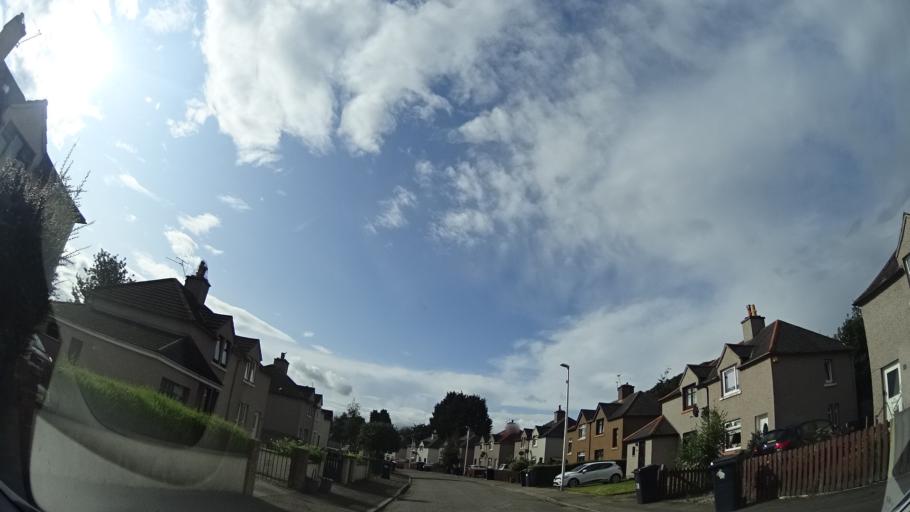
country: GB
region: Scotland
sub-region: Highland
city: Inverness
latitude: 57.4709
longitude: -4.2395
